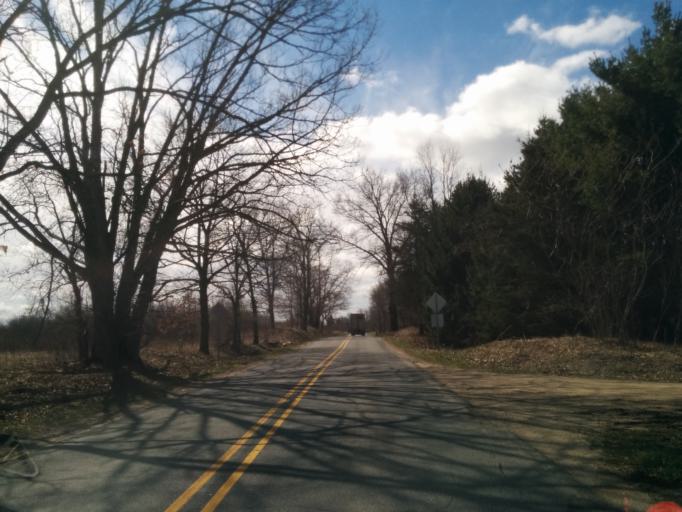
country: US
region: Michigan
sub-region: Newaygo County
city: Newaygo
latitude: 43.4226
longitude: -85.6423
